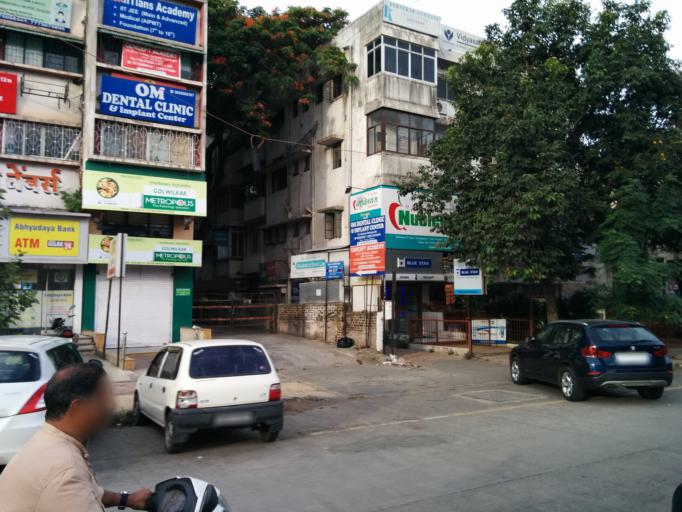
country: IN
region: Maharashtra
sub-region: Pune Division
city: Pune
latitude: 18.5088
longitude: 73.8222
